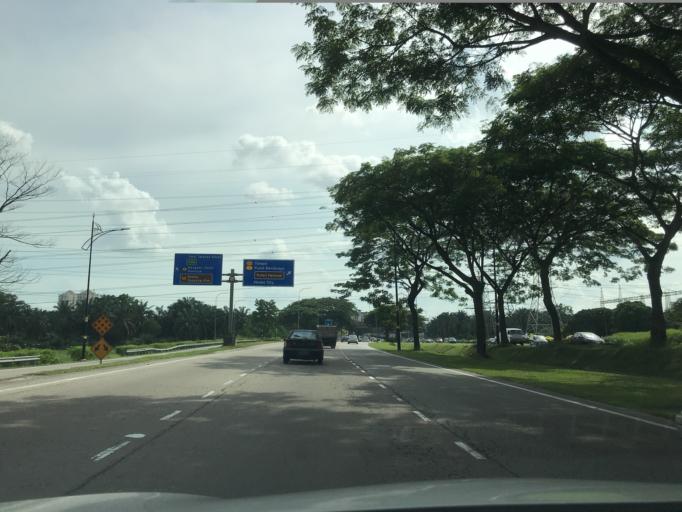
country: MY
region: Johor
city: Skudai
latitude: 1.5533
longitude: 103.6587
